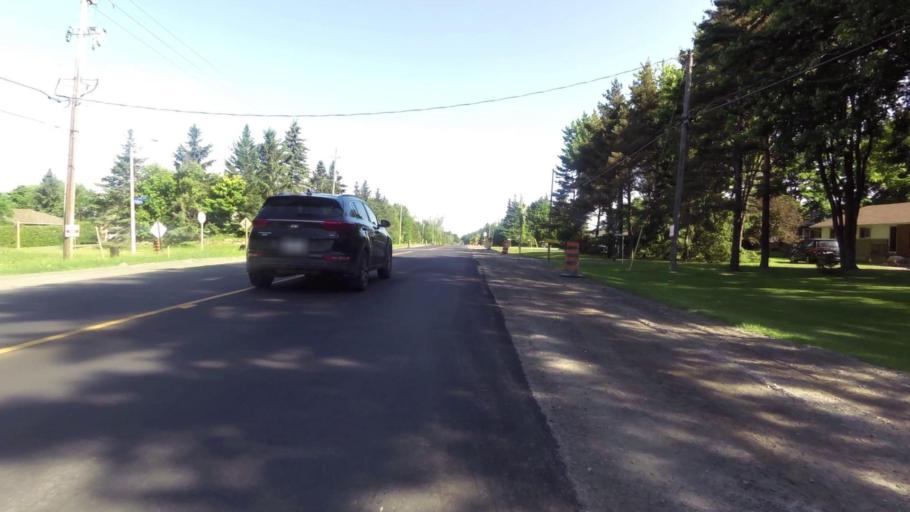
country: CA
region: Ontario
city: Ottawa
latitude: 45.2511
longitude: -75.5907
